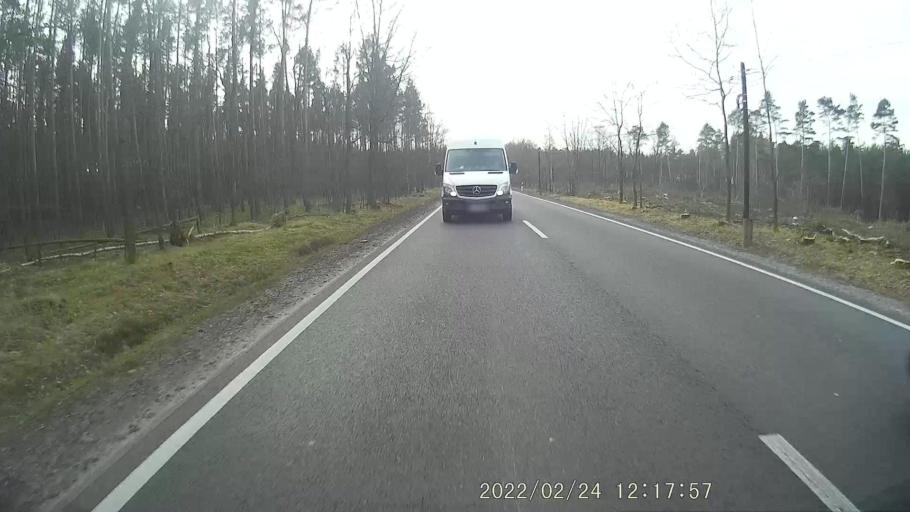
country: PL
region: Lower Silesian Voivodeship
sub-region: Powiat glogowski
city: Glogow
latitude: 51.6498
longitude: 16.0724
